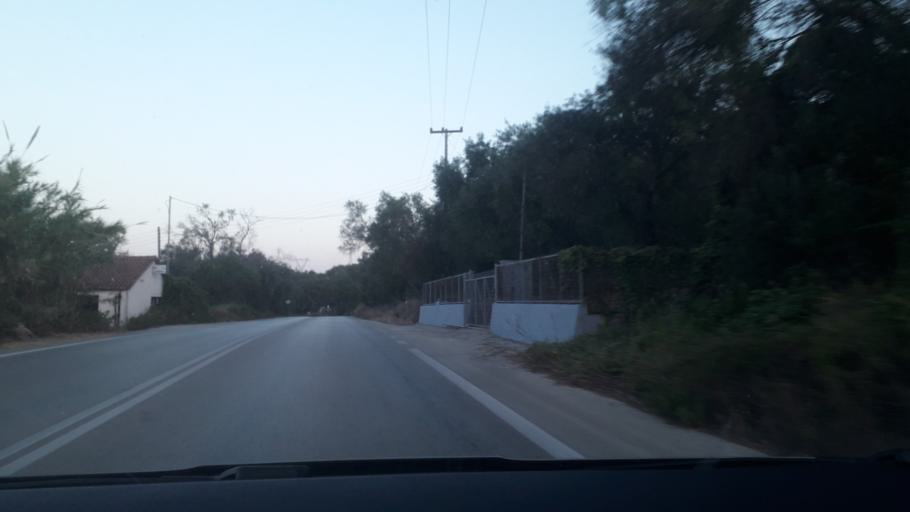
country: GR
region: Ionian Islands
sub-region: Nomos Kerkyras
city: Perivoli
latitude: 39.4432
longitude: 19.9530
